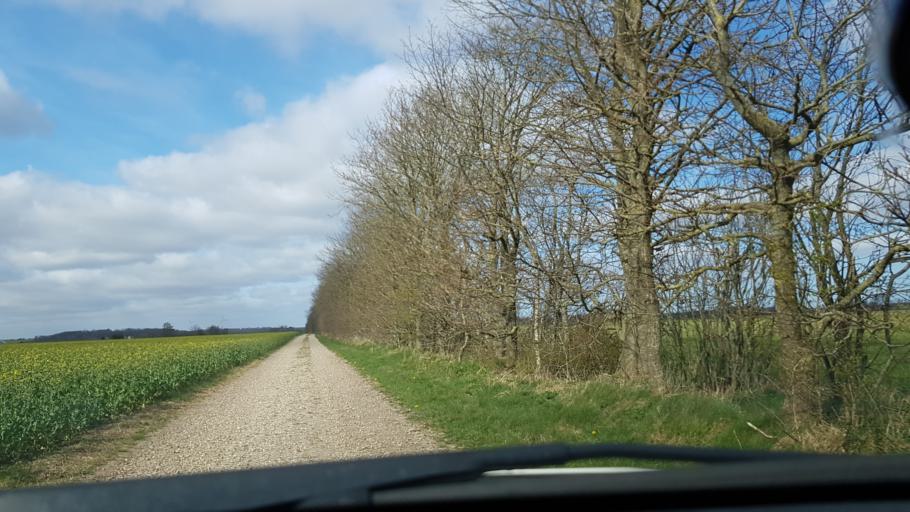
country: DK
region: South Denmark
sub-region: Vejen Kommune
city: Rodding
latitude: 55.3696
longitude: 8.9661
